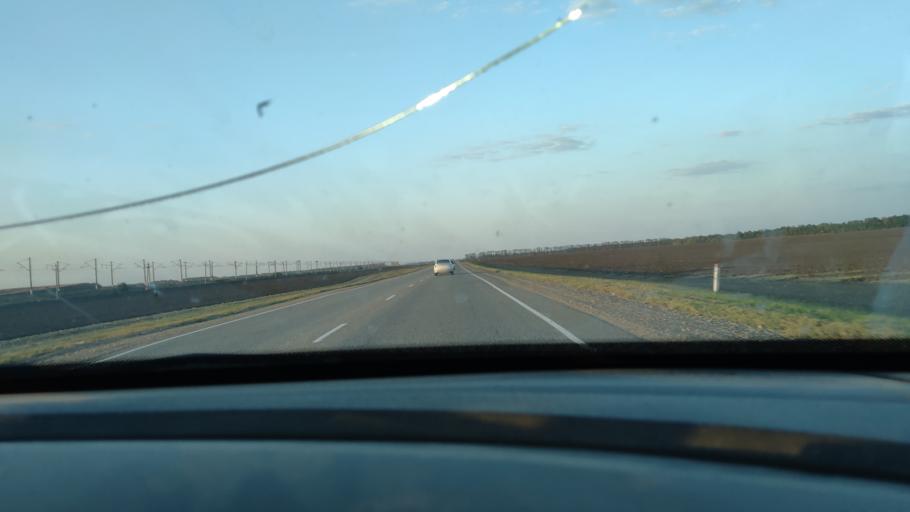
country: RU
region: Krasnodarskiy
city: Novominskaya
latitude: 46.3362
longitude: 38.9480
